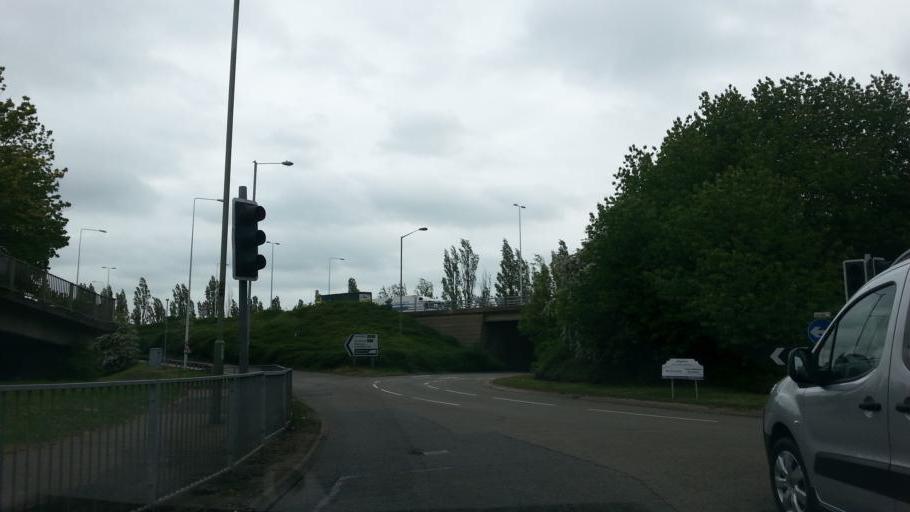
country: GB
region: England
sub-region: Peterborough
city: Peterborough
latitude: 52.5976
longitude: -0.2618
